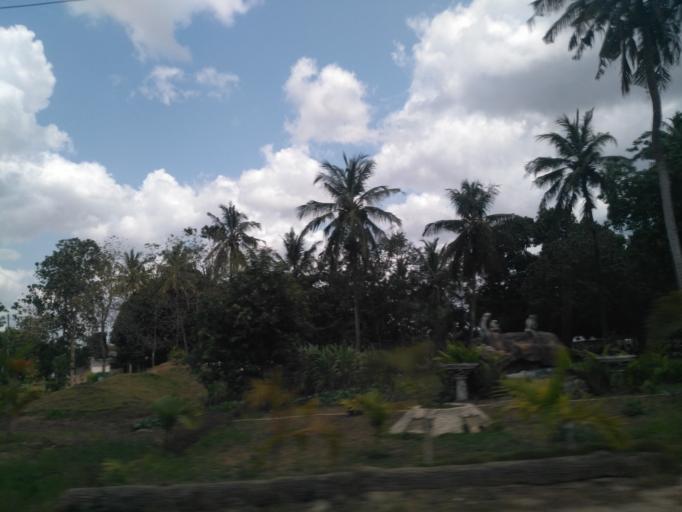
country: TZ
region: Dar es Salaam
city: Dar es Salaam
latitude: -6.8716
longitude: 39.3462
